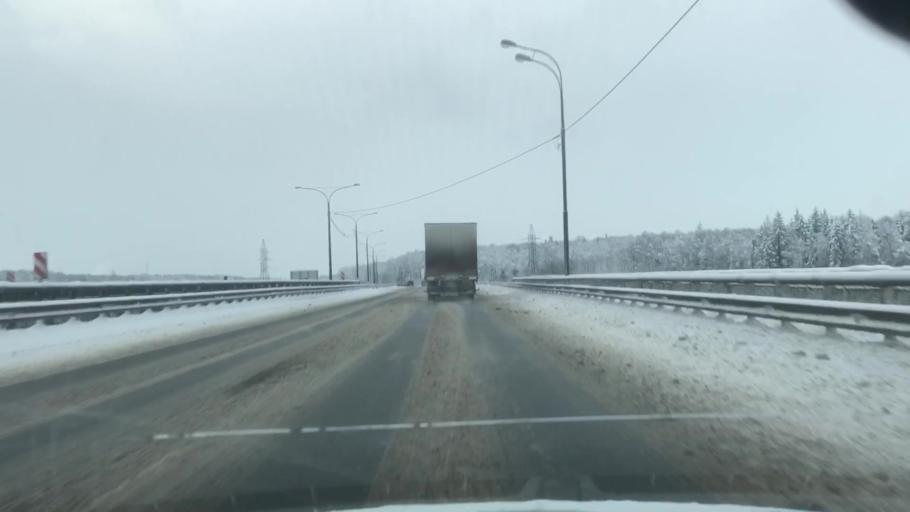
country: RU
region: Moskovskaya
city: Mikhnevo
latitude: 55.1436
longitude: 37.9314
